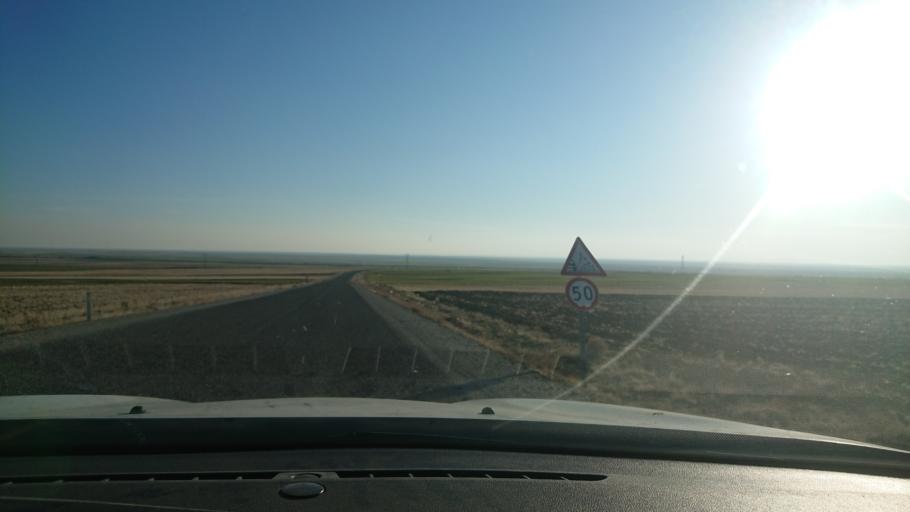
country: TR
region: Aksaray
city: Acipinar
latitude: 38.6788
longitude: 33.7332
